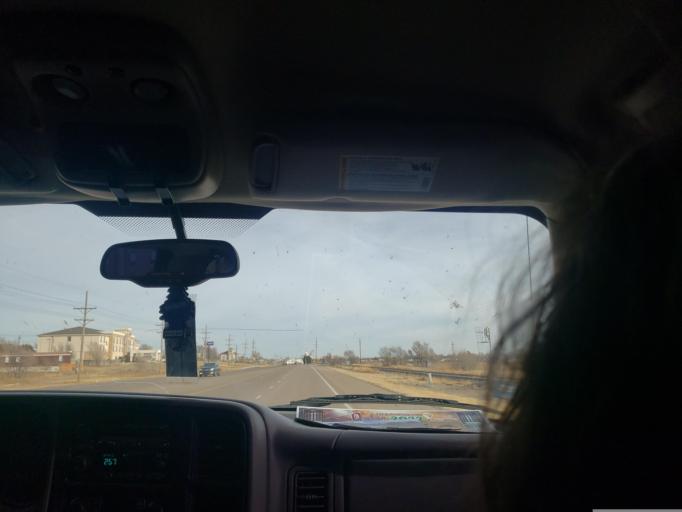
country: US
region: Kansas
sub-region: Ford County
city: Dodge City
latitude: 37.7545
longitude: -100.0559
